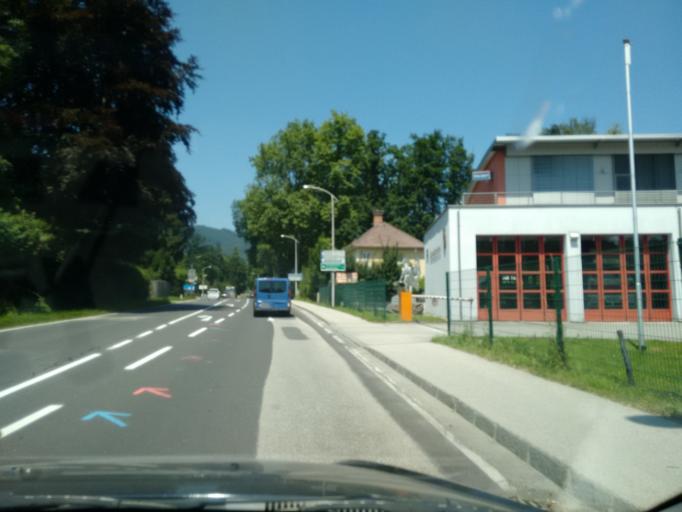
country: AT
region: Upper Austria
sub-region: Politischer Bezirk Gmunden
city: Altmunster
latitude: 47.8952
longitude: 13.7658
